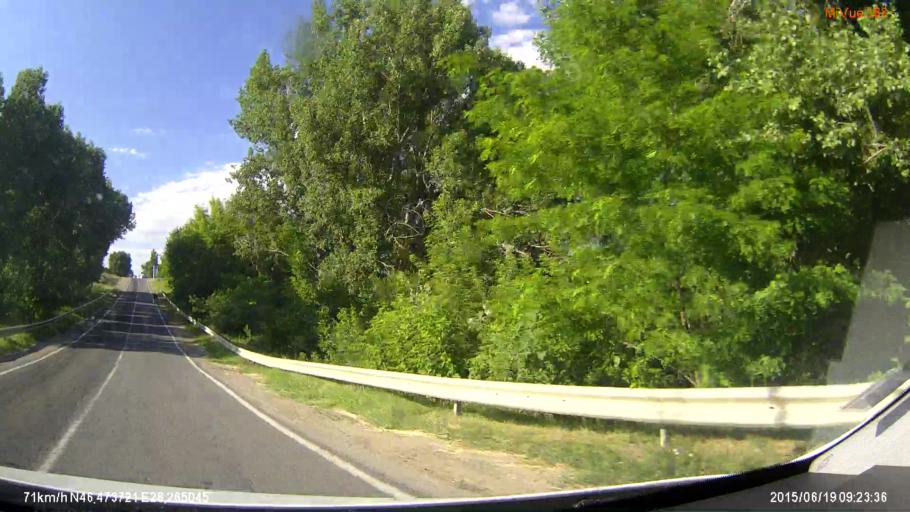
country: MD
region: Leova
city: Leova
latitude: 46.4735
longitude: 28.2650
